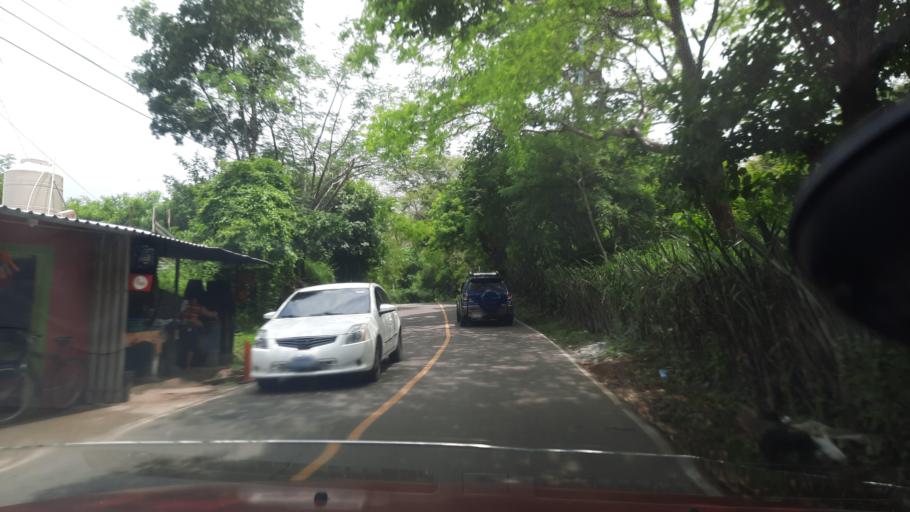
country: SV
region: La Union
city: Santa Rosa de Lima
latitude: 13.6483
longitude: -87.8492
